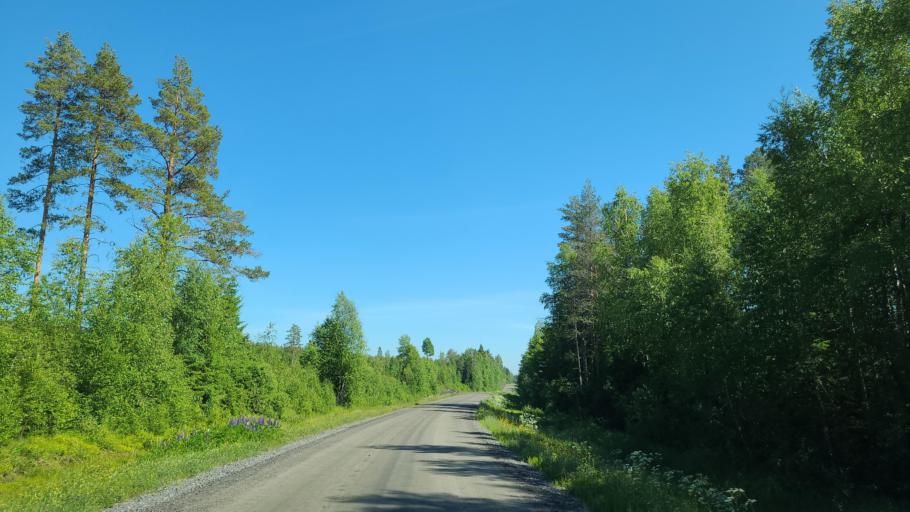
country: SE
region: Vaesterbotten
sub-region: Bjurholms Kommun
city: Bjurholm
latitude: 63.6428
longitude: 19.1229
